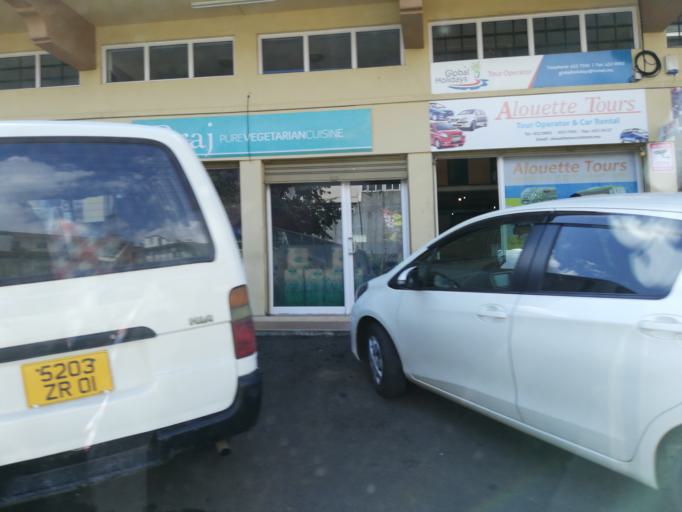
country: MU
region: Moka
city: Verdun
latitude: -20.2244
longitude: 57.5407
